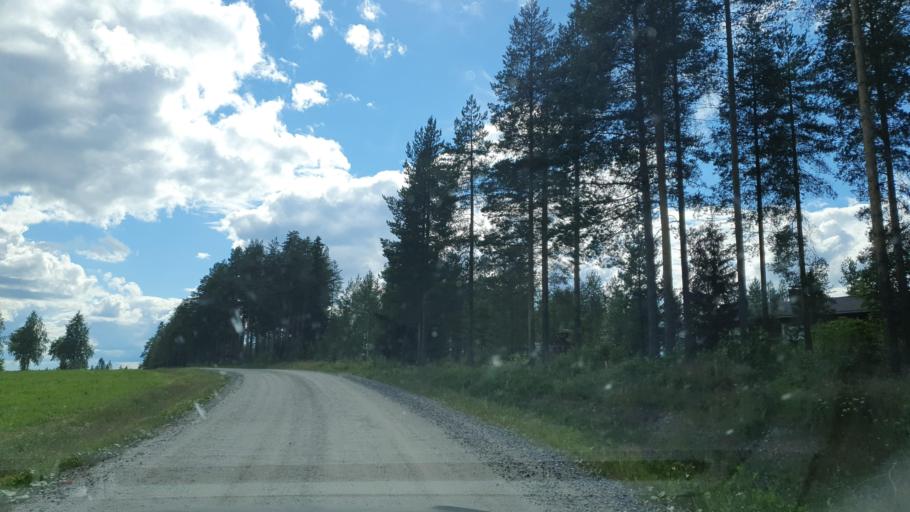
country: FI
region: Kainuu
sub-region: Kehys-Kainuu
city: Kuhmo
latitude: 64.1287
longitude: 29.6458
